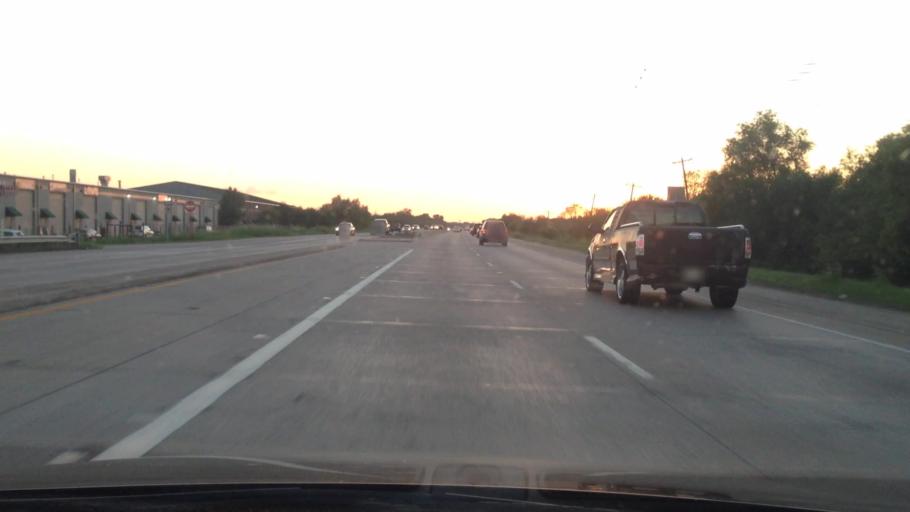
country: US
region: Texas
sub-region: Denton County
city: Lewisville
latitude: 33.0475
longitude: -96.9478
